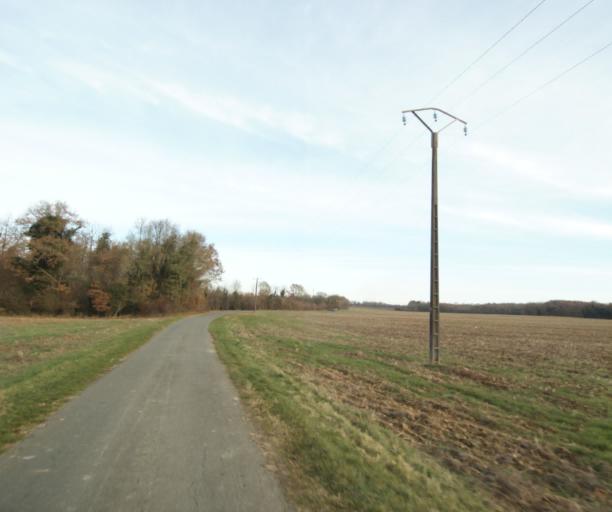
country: FR
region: Poitou-Charentes
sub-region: Departement de la Charente-Maritime
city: Saint-Hilaire-de-Villefranche
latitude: 45.8352
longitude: -0.5735
